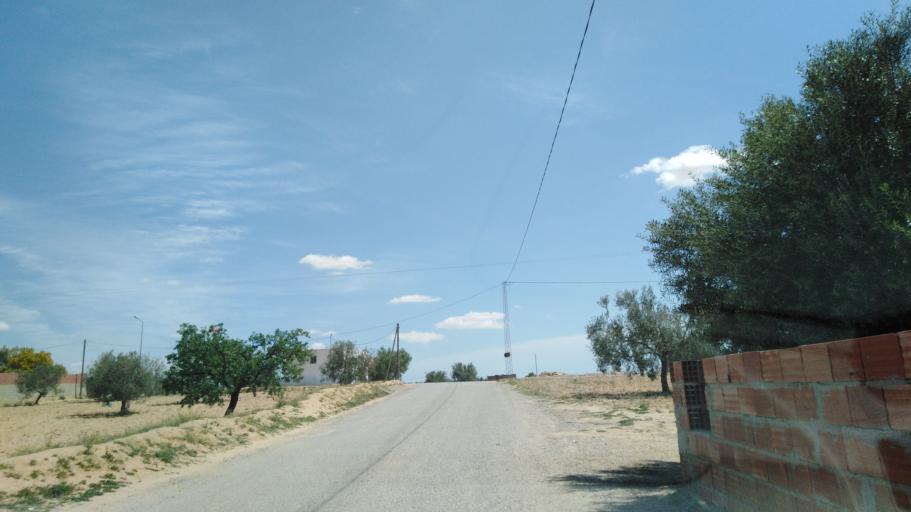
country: TN
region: Safaqis
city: Sfax
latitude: 34.7445
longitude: 10.5507
